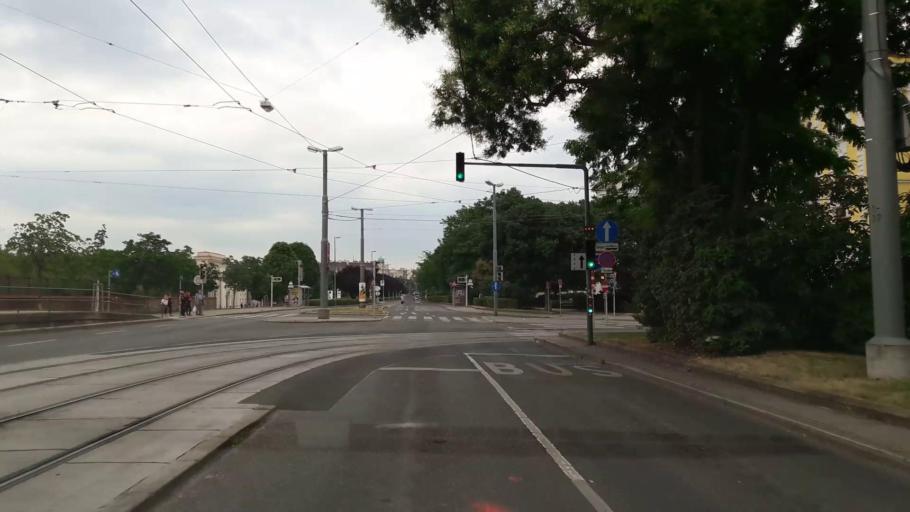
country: AT
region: Vienna
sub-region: Wien Stadt
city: Vienna
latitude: 48.2231
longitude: 16.3751
